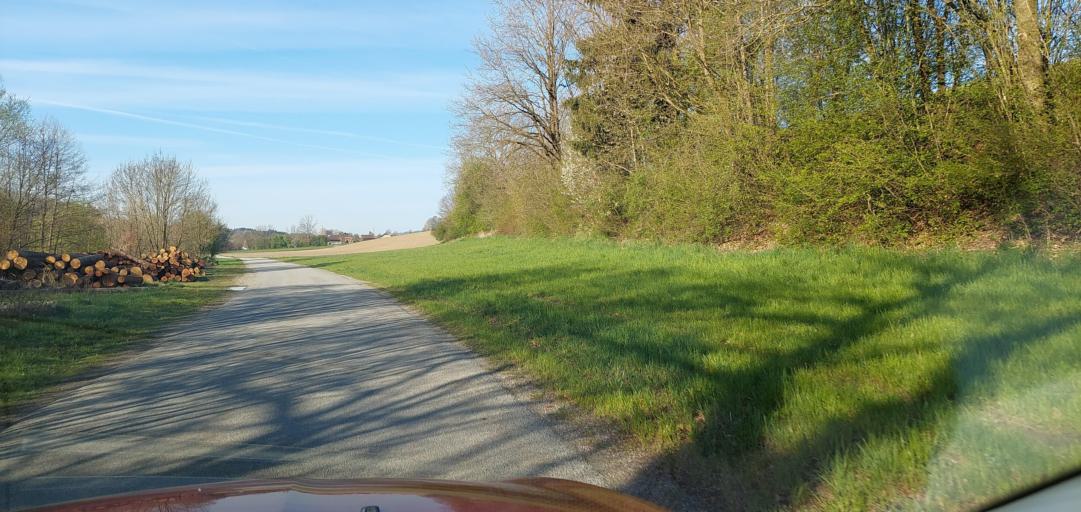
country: AT
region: Upper Austria
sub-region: Wels-Land
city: Offenhausen
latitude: 48.1697
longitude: 13.8033
